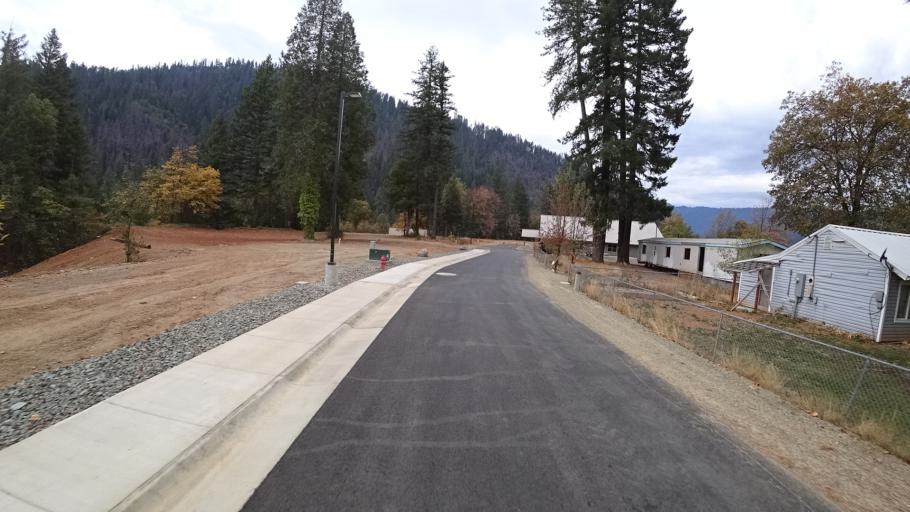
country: US
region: California
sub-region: Siskiyou County
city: Happy Camp
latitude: 41.7936
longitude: -123.3753
